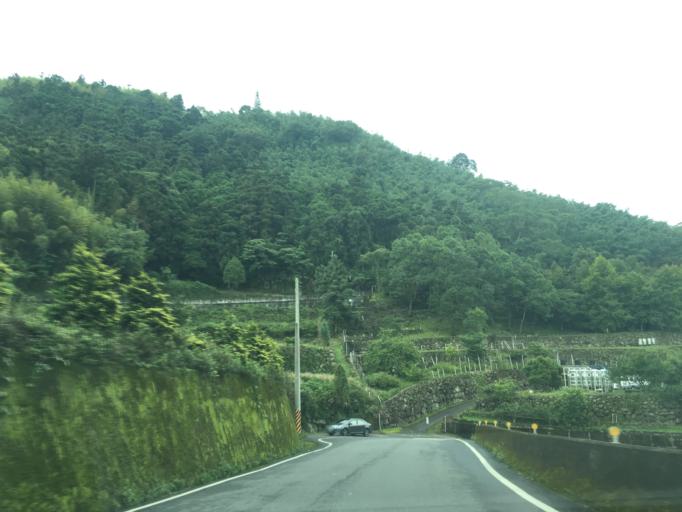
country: TW
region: Taiwan
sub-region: Chiayi
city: Jiayi Shi
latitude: 23.4475
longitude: 120.6664
